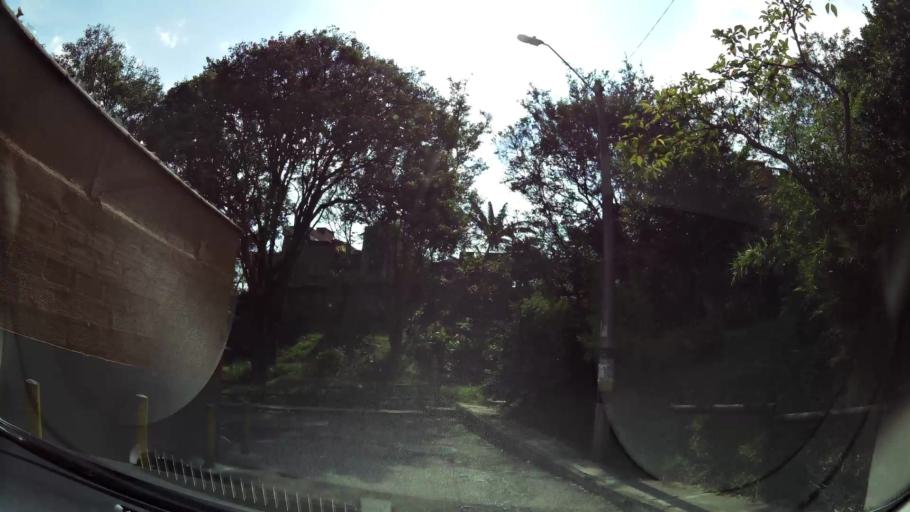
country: CO
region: Antioquia
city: Medellin
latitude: 6.2852
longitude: -75.5941
